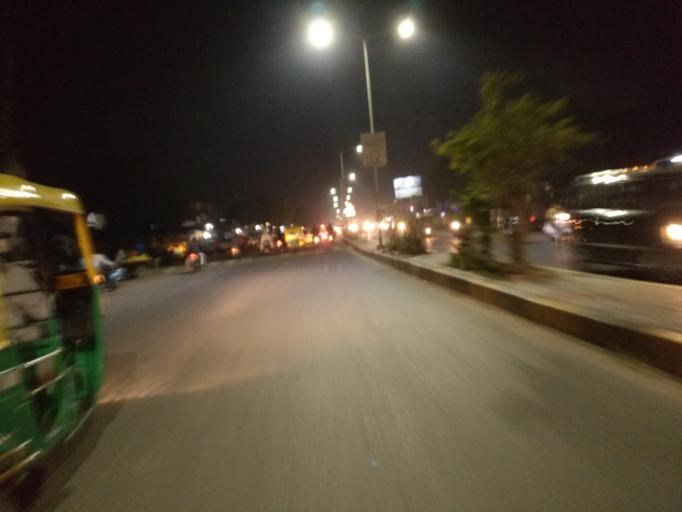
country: IN
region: Gujarat
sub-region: Ahmadabad
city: Sarkhej
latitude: 22.9990
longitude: 72.5446
